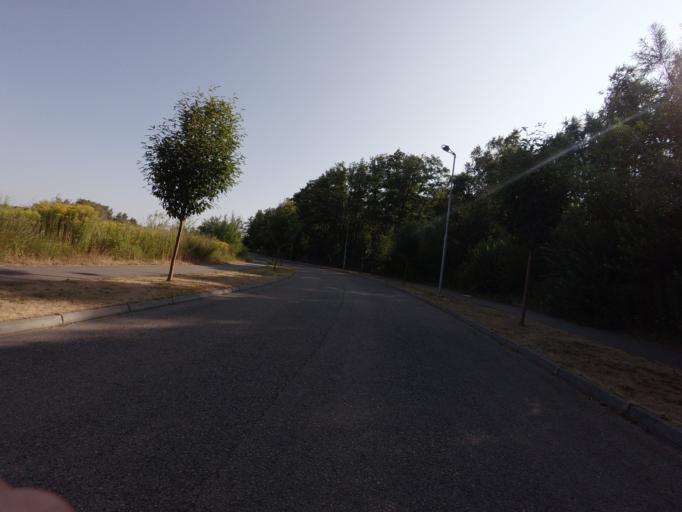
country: SE
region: Skane
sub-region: Landskrona
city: Asmundtorp
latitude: 55.8459
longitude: 12.9294
